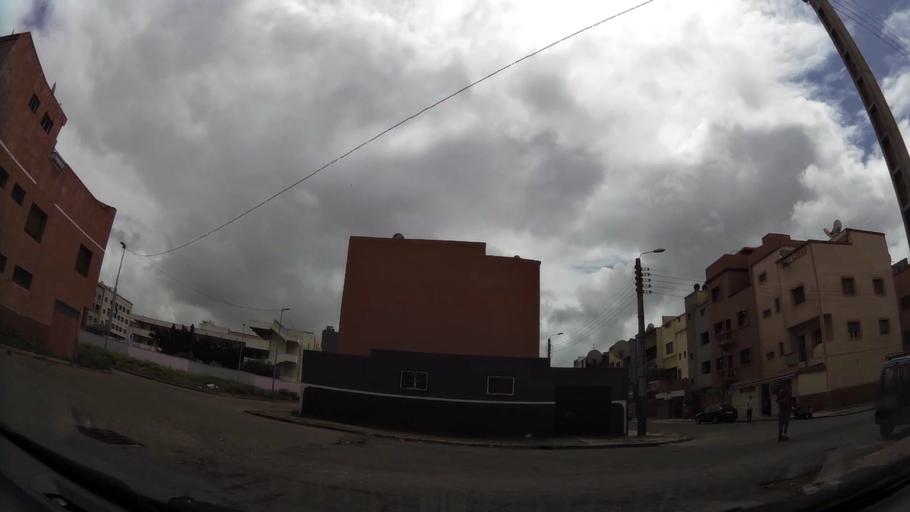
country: MA
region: Grand Casablanca
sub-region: Casablanca
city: Casablanca
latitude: 33.5352
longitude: -7.5999
